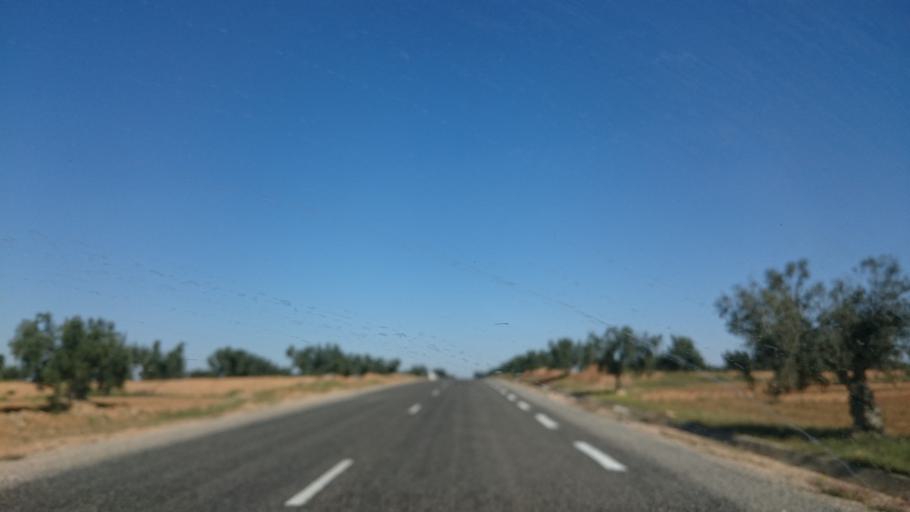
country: TN
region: Safaqis
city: Sfax
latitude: 34.8276
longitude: 10.4674
